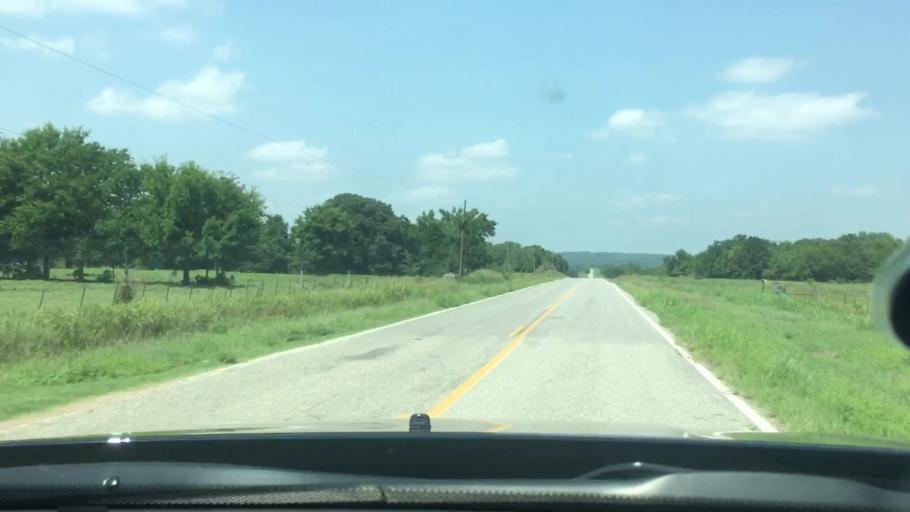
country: US
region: Oklahoma
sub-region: Johnston County
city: Tishomingo
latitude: 34.3844
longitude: -96.4962
